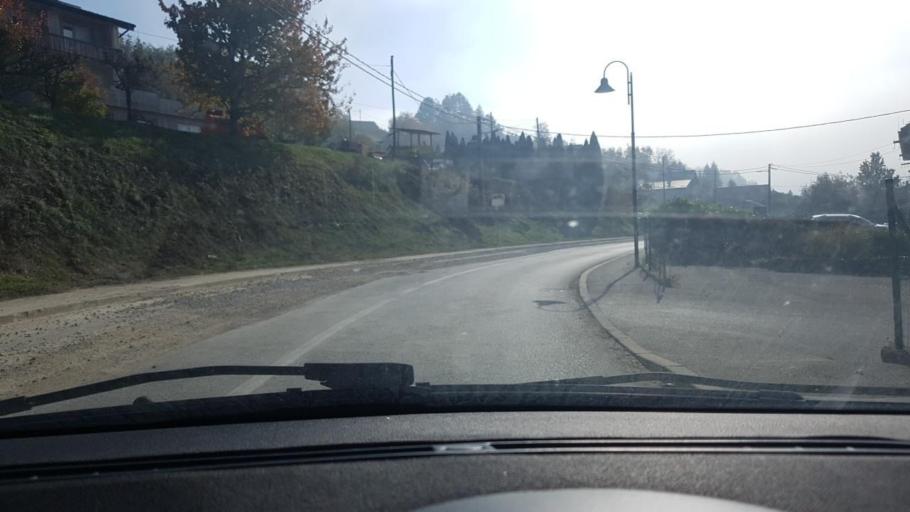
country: HR
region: Krapinsko-Zagorska
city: Zlatar
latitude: 46.1489
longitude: 16.0669
